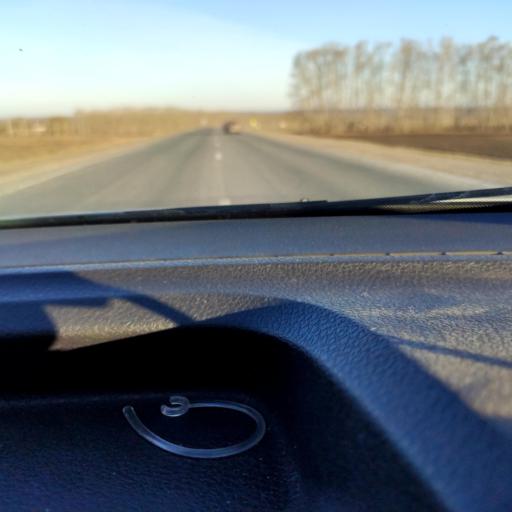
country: RU
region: Bashkortostan
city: Kabakovo
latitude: 54.4723
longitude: 55.9251
